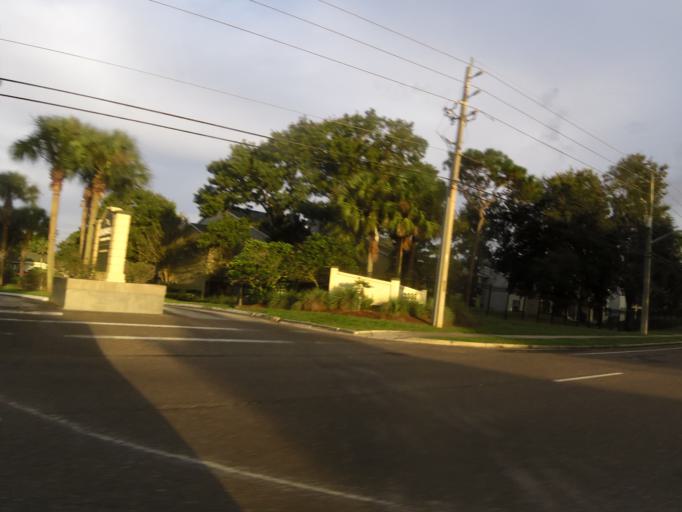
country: US
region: Florida
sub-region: Duval County
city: Atlantic Beach
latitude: 30.3661
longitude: -81.5030
